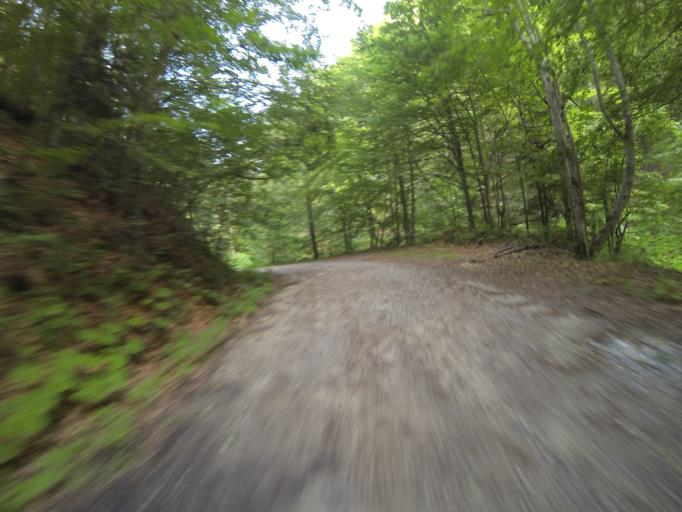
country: RO
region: Valcea
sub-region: Oras Baile Olanesti
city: Baile Olanesti
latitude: 45.2435
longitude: 24.1856
